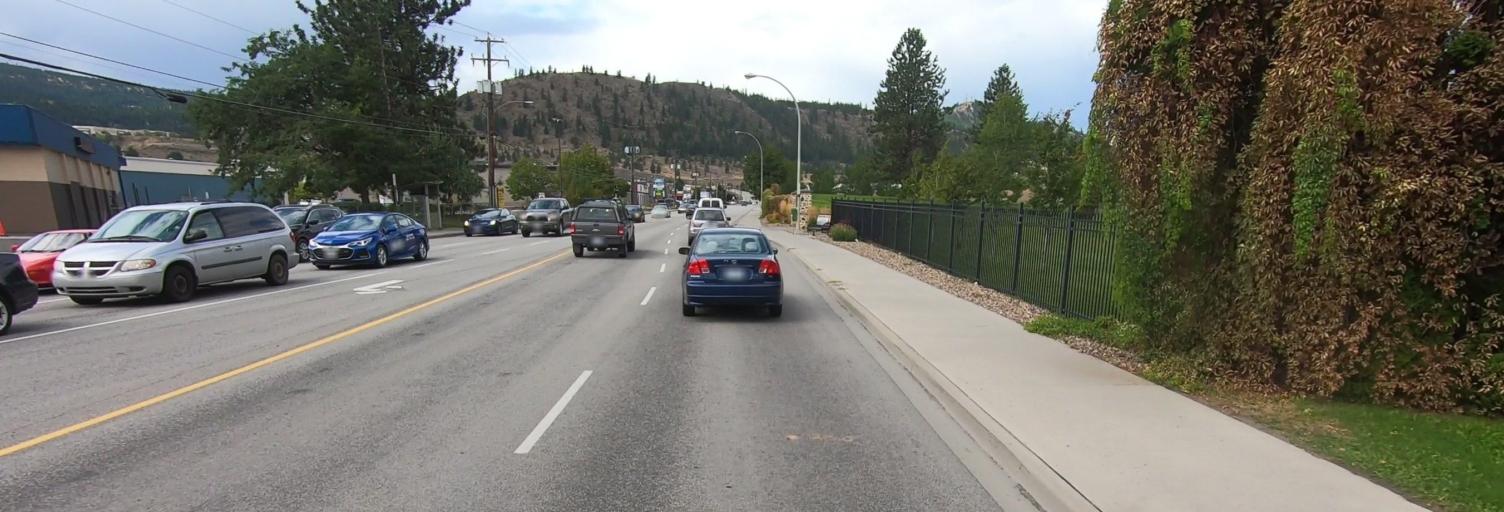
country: CA
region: British Columbia
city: Kamloops
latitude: 50.6637
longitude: -120.3561
